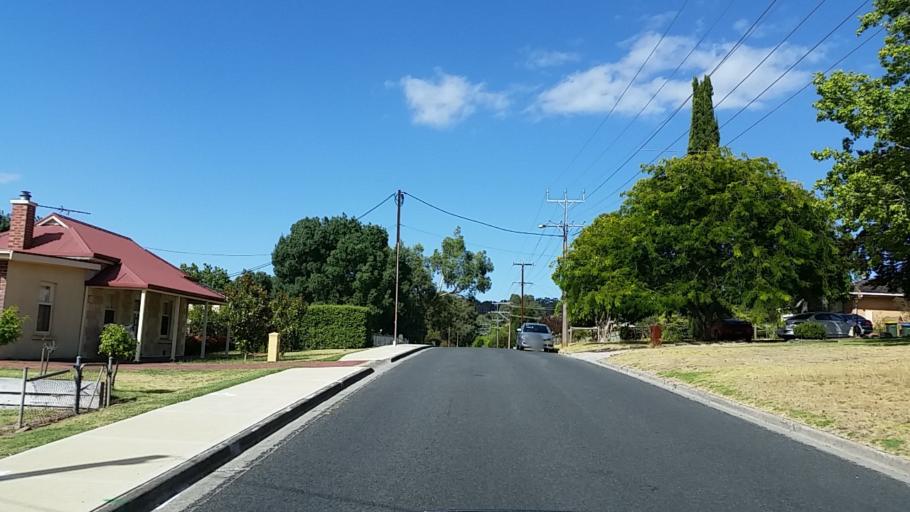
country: AU
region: South Australia
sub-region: Mount Barker
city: Hahndorf
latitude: -35.0312
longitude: 138.8151
